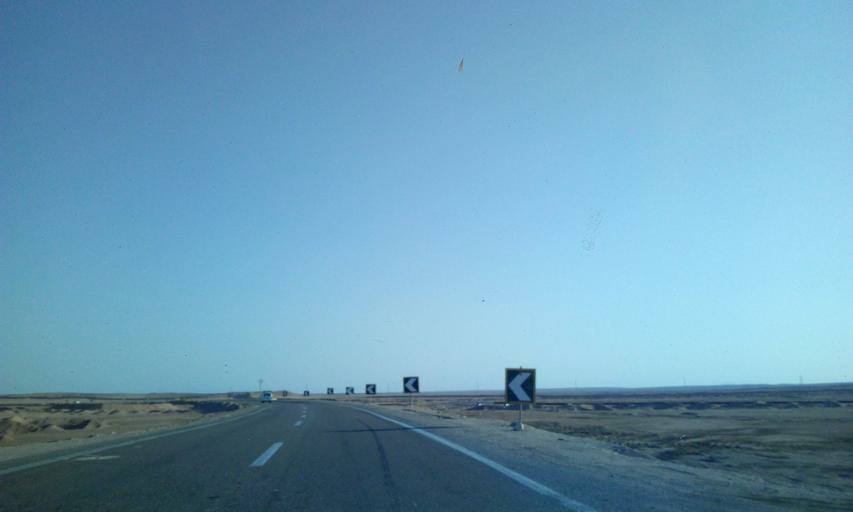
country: EG
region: South Sinai
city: Tor
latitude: 28.5754
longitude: 32.8616
